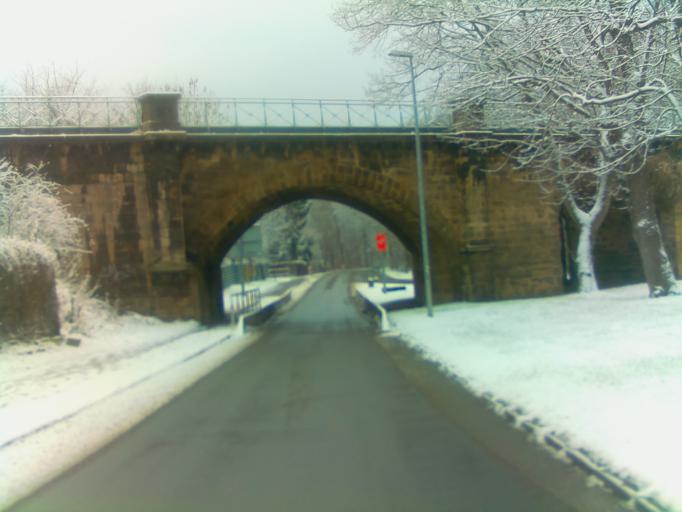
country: DE
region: Thuringia
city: Arnstadt
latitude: 50.8374
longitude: 10.9583
